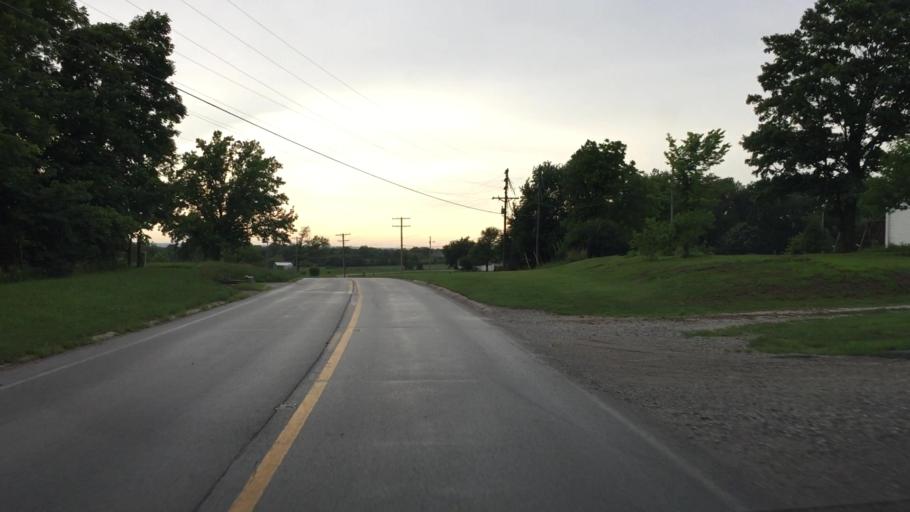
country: US
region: Illinois
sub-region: Hancock County
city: Warsaw
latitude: 40.3556
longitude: -91.4091
